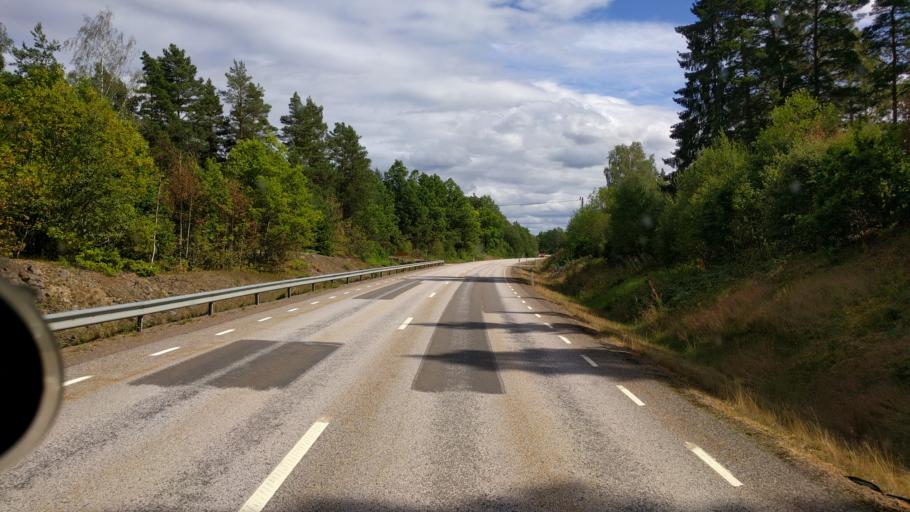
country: SE
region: Kalmar
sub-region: Vasterviks Kommun
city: Ankarsrum
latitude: 57.7187
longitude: 16.0892
